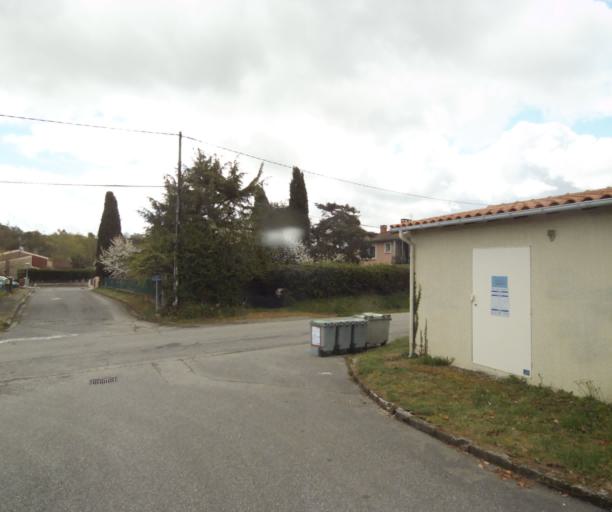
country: FR
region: Midi-Pyrenees
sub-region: Departement de l'Ariege
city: Saverdun
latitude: 43.2273
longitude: 1.5712
